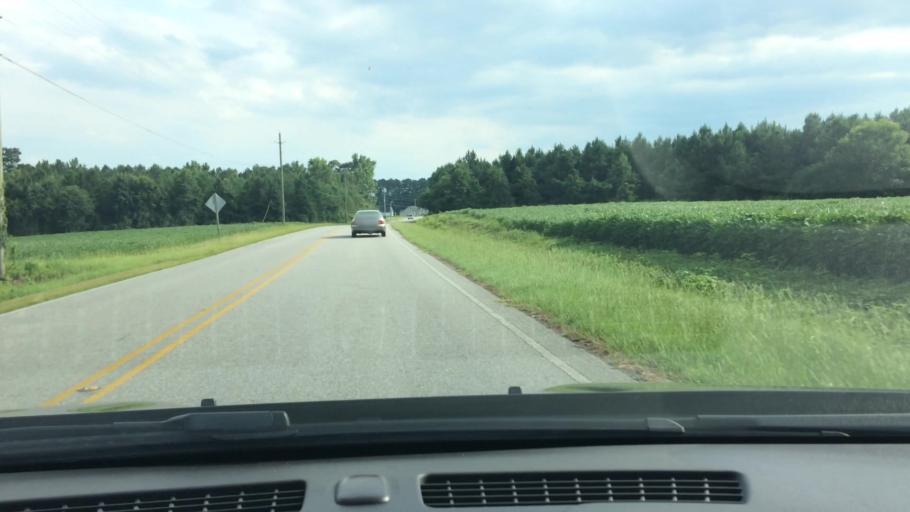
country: US
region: North Carolina
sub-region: Pitt County
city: Ayden
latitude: 35.4803
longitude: -77.3776
